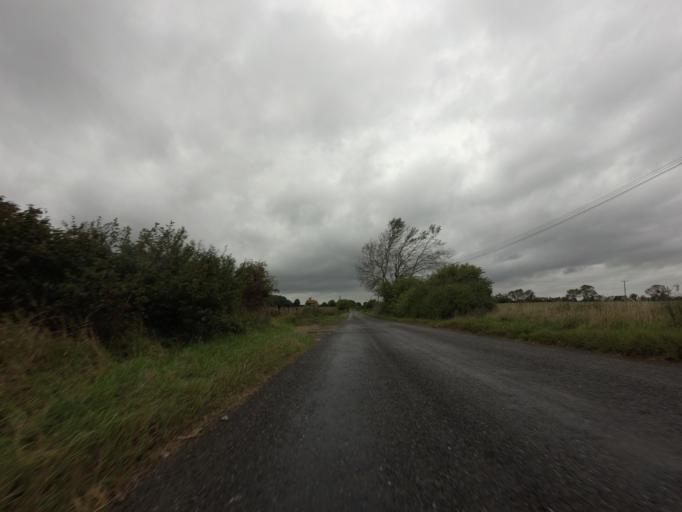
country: GB
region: England
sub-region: Cambridgeshire
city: Wimpole
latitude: 52.1737
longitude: -0.0248
